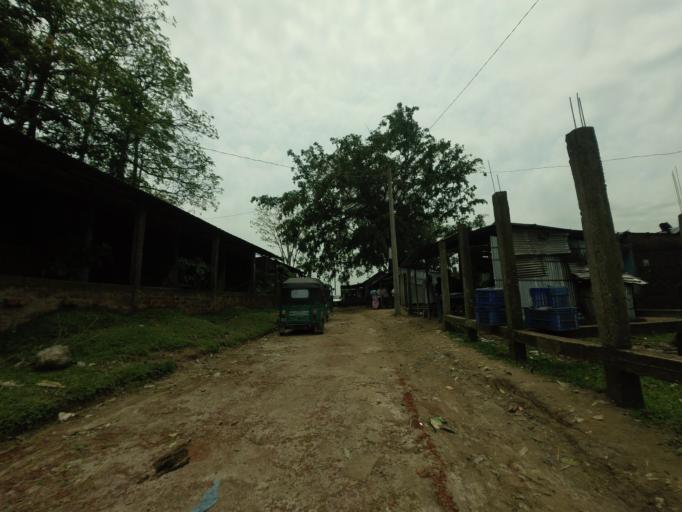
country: BD
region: Sylhet
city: Sylhet
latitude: 25.0064
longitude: 91.9164
